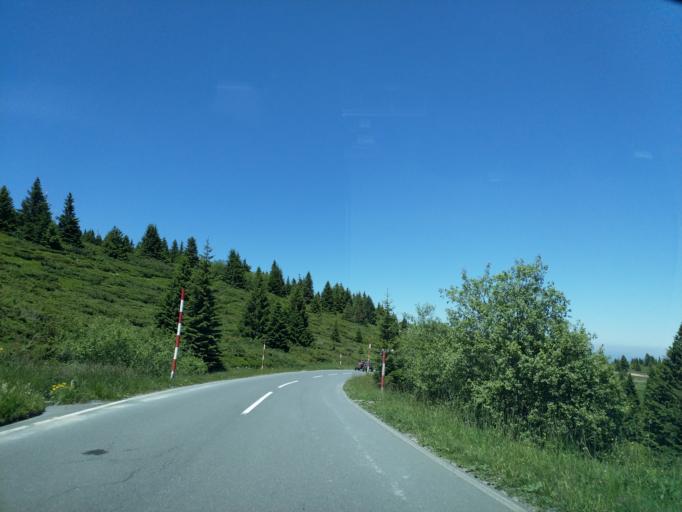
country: XK
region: Mitrovica
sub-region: Komuna e Leposaviqit
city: Leposaviq
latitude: 43.3110
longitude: 20.8309
